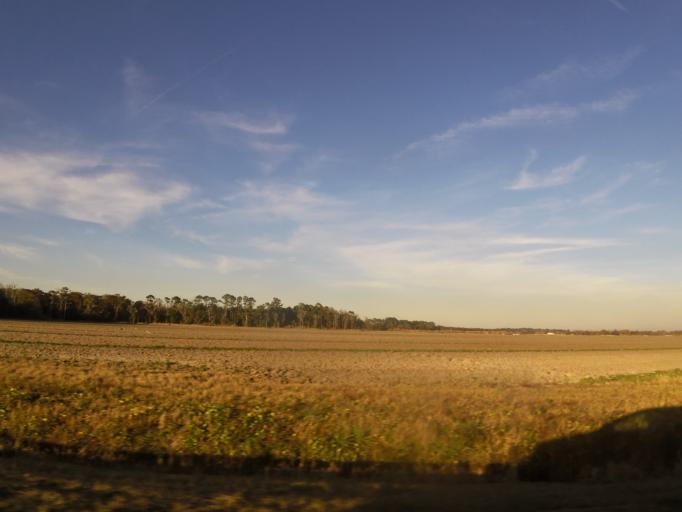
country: US
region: Florida
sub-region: Putnam County
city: East Palatka
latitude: 29.7939
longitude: -81.5036
